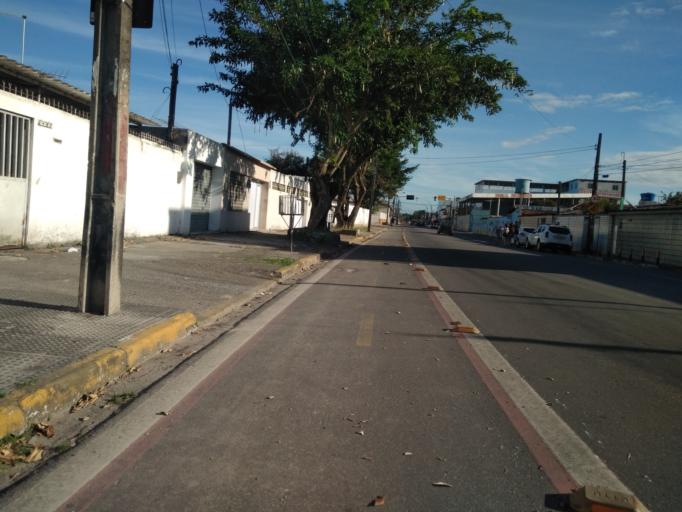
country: BR
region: Pernambuco
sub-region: Recife
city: Recife
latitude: -8.0726
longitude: -34.9292
